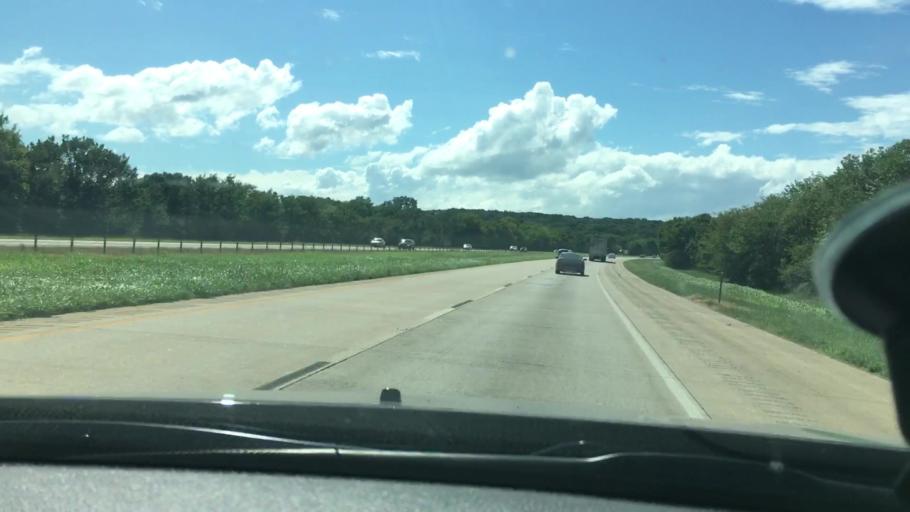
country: US
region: Oklahoma
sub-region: Sequoyah County
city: Vian
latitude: 35.4897
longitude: -95.0304
